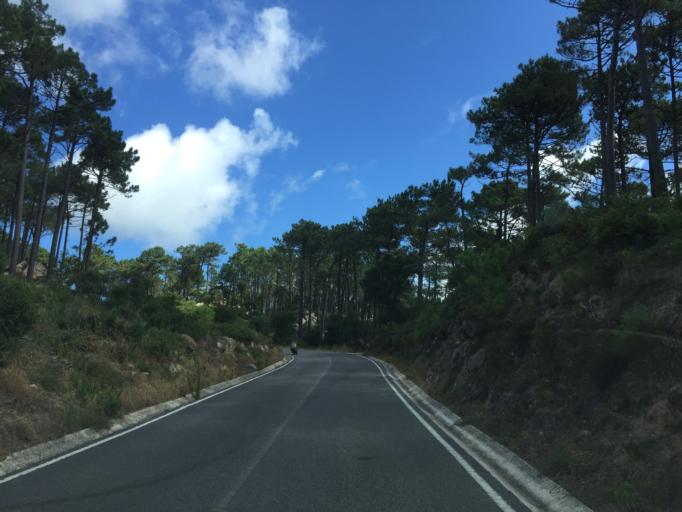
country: PT
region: Lisbon
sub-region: Cascais
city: Alcabideche
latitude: 38.7570
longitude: -9.4279
